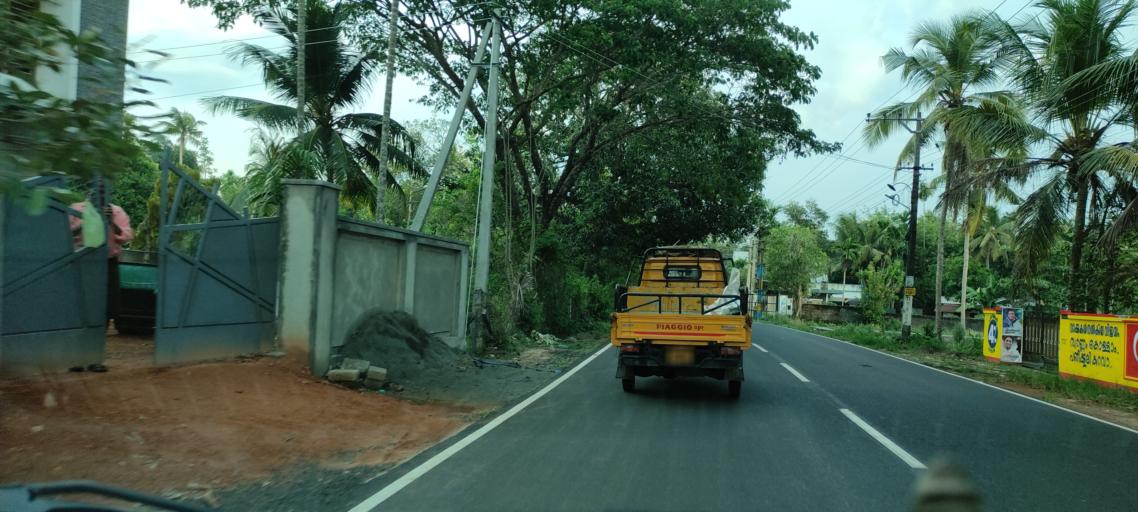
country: IN
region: Kerala
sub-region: Alappuzha
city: Kutiatodu
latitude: 9.8253
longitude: 76.3436
